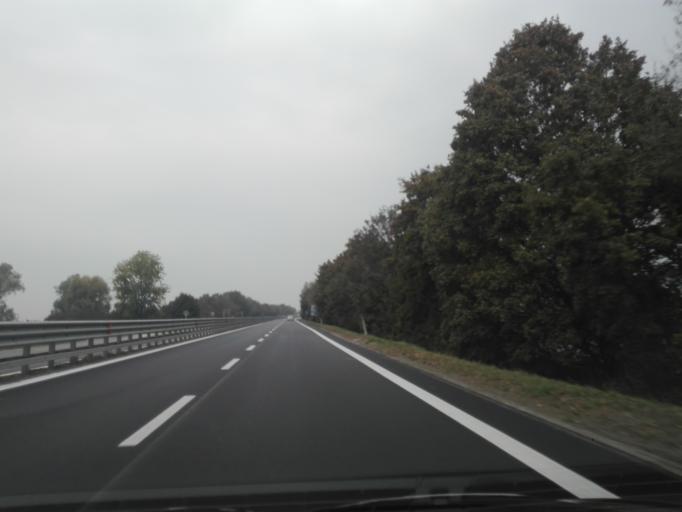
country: IT
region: Veneto
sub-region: Provincia di Verona
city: Villa Bartolomea
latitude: 45.1615
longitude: 11.3089
